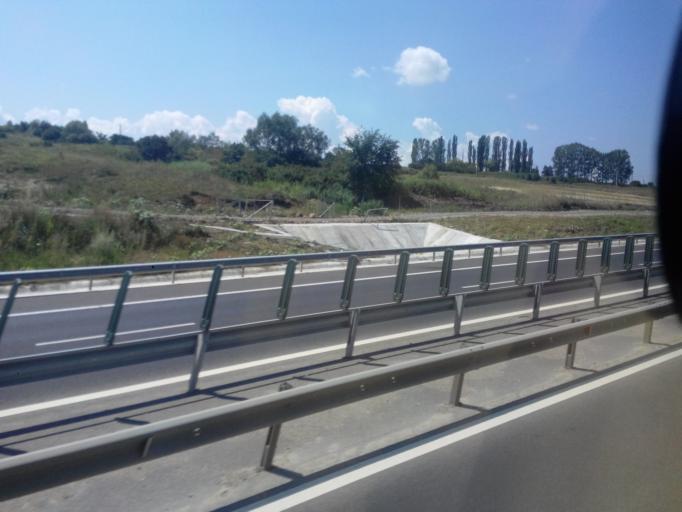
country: RO
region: Alba
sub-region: Comuna Cut
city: Cut
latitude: 45.9223
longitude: 23.6683
